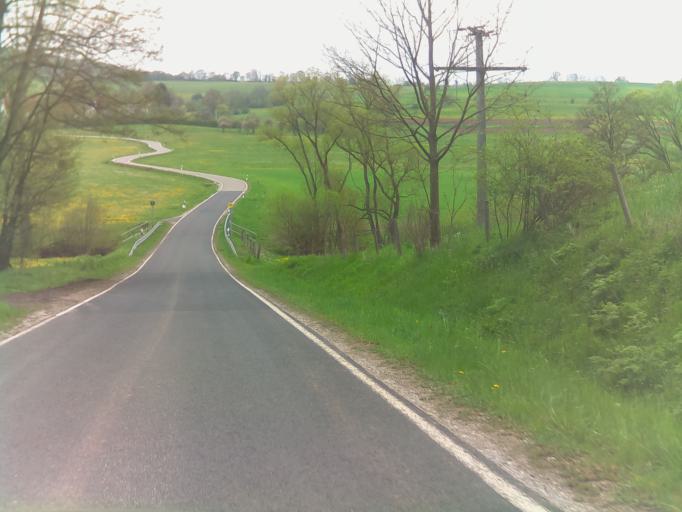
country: DE
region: Hesse
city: Tann
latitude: 50.6198
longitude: 10.0378
